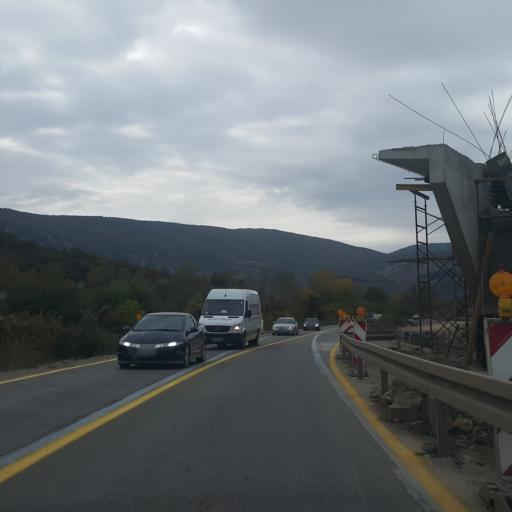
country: RS
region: Central Serbia
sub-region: Pirotski Okrug
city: Pirot
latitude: 43.2157
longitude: 22.5345
